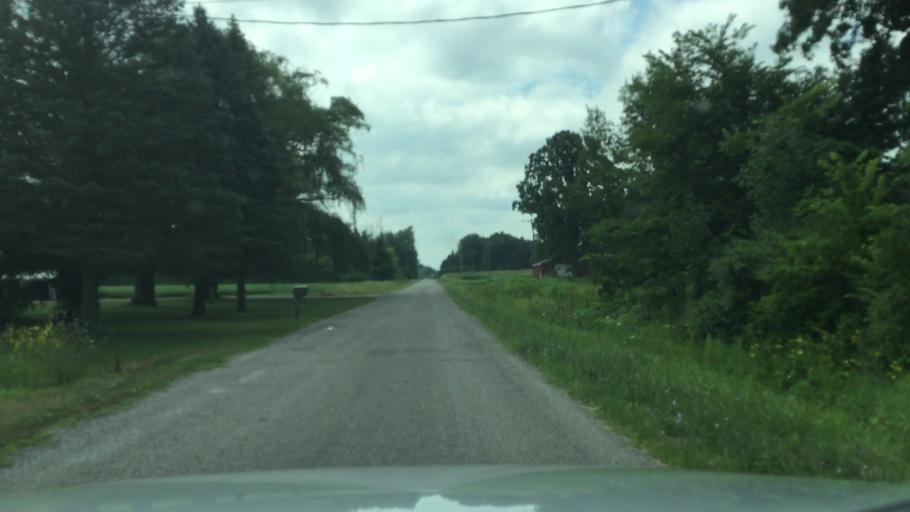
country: US
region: Michigan
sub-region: Saginaw County
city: Birch Run
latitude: 43.2999
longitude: -83.8347
